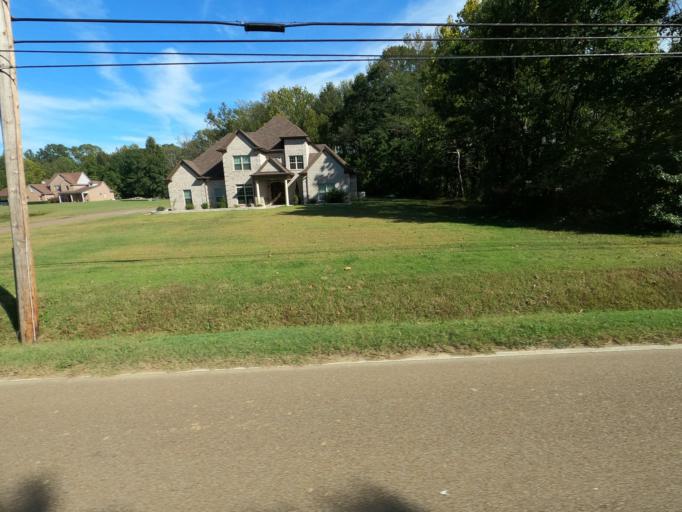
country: US
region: Tennessee
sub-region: Fayette County
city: Hickory Withe
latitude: 35.2330
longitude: -89.6500
